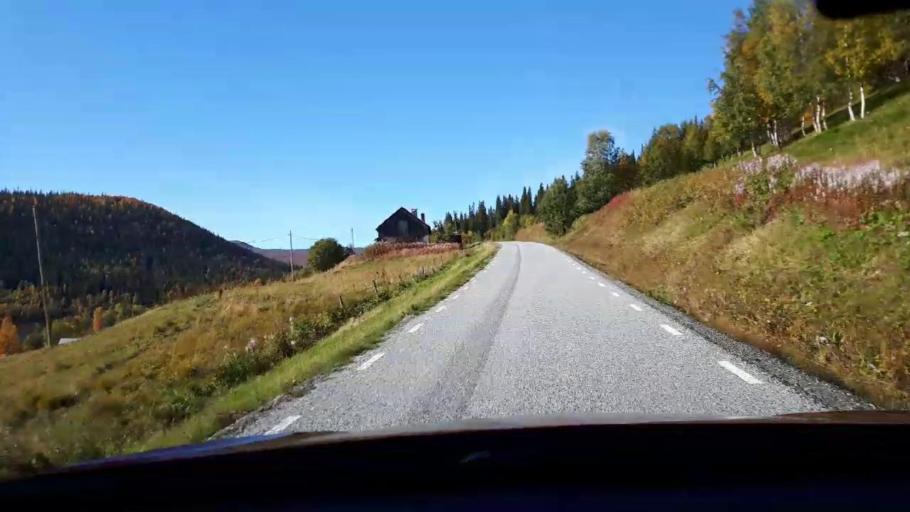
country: NO
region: Nord-Trondelag
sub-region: Royrvik
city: Royrvik
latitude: 64.8766
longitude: 14.2306
